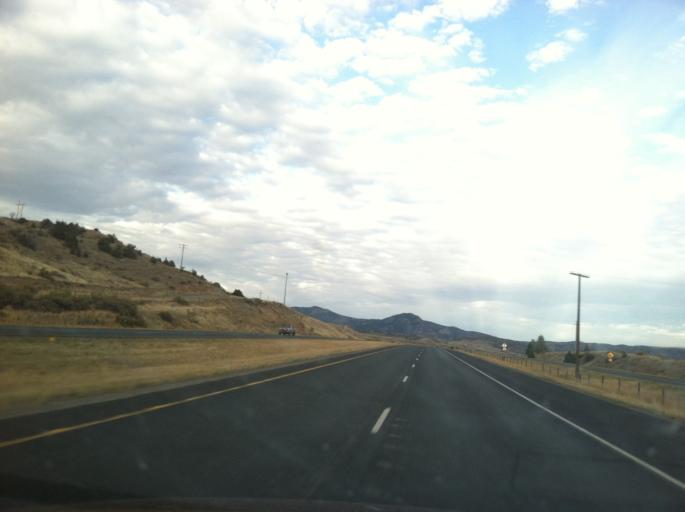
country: US
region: Montana
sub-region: Jefferson County
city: Whitehall
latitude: 45.8718
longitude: -112.0354
